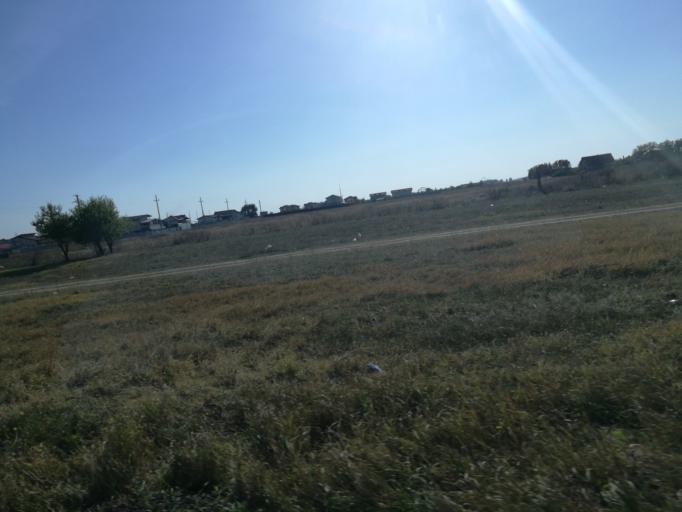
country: RO
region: Giurgiu
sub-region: Comuna Joita
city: Bacu
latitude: 44.4764
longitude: 25.9055
